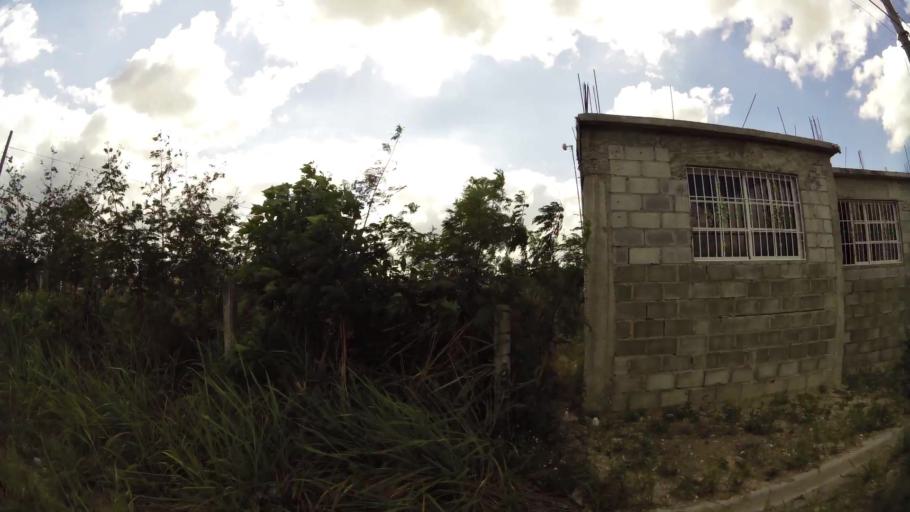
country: DO
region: Nacional
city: Ensanche Luperon
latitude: 18.5294
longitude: -69.8950
